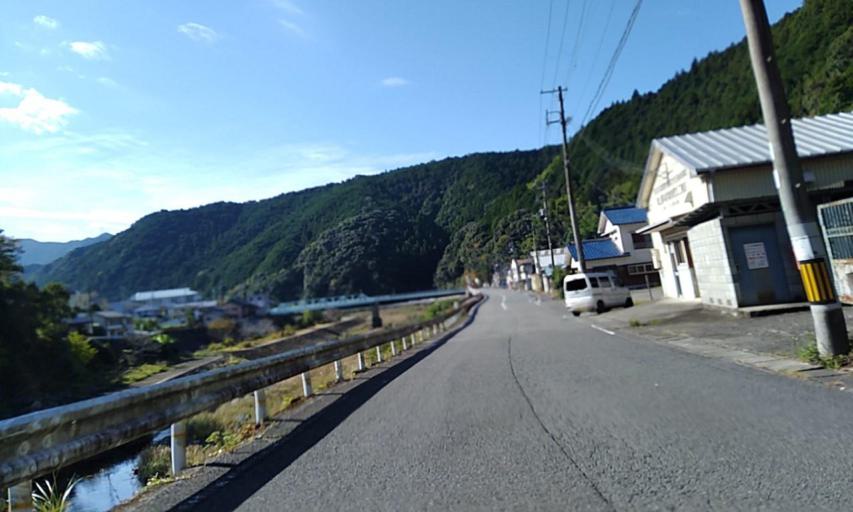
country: JP
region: Wakayama
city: Kainan
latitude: 34.0728
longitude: 135.3574
